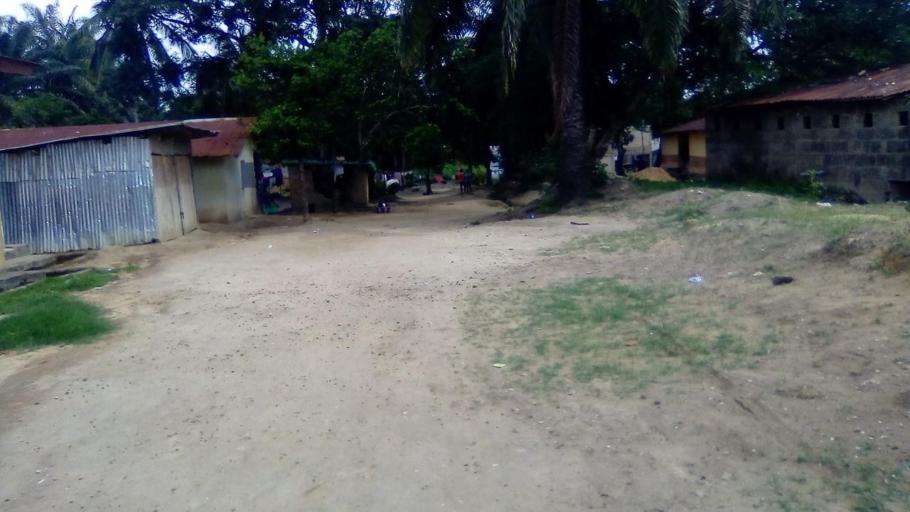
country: SL
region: Southern Province
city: Bo
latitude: 7.9583
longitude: -11.7216
